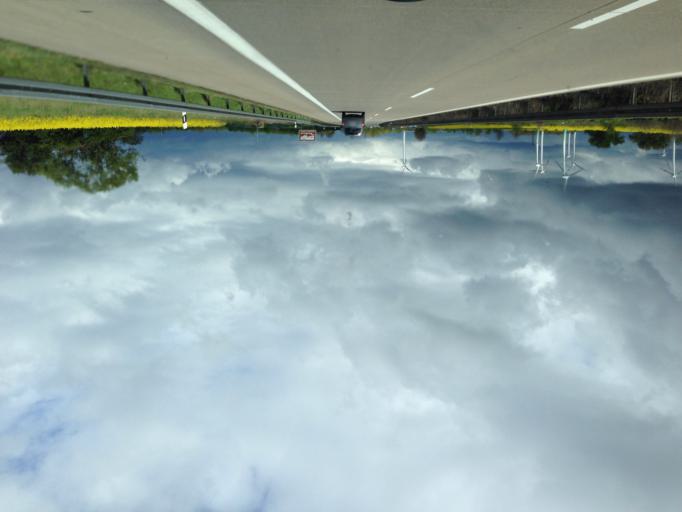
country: DE
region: Saxony-Anhalt
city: Nauendorf
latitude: 51.6100
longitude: 11.8705
